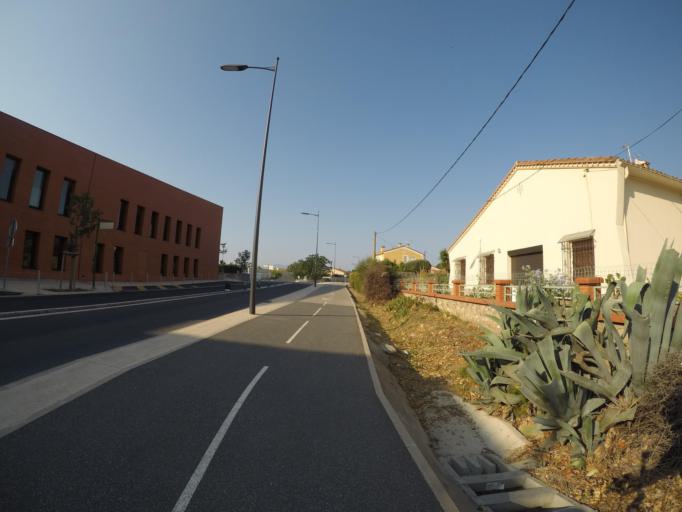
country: FR
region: Languedoc-Roussillon
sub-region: Departement des Pyrenees-Orientales
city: Canohes
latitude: 42.6520
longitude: 2.8308
